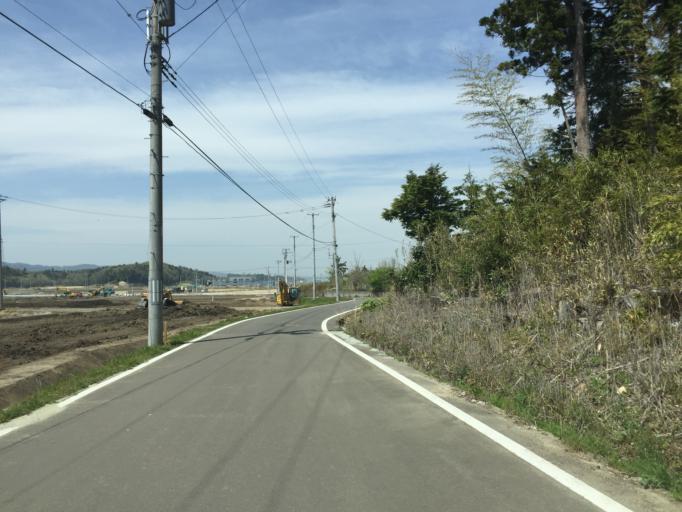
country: JP
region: Miyagi
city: Watari
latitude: 37.8980
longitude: 140.9264
